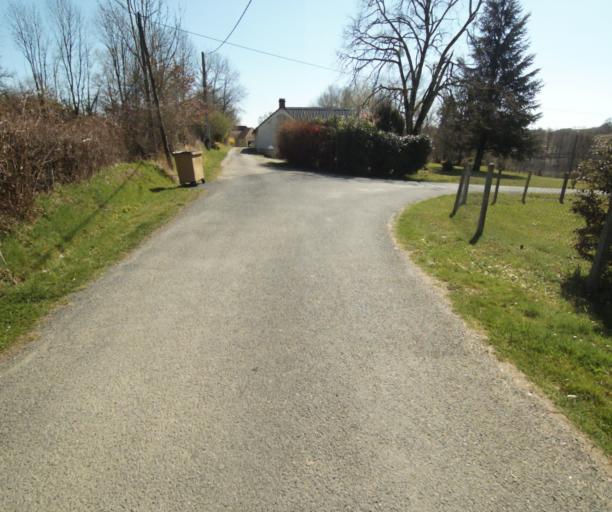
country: FR
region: Limousin
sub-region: Departement de la Correze
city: Saint-Clement
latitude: 45.3204
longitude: 1.6960
